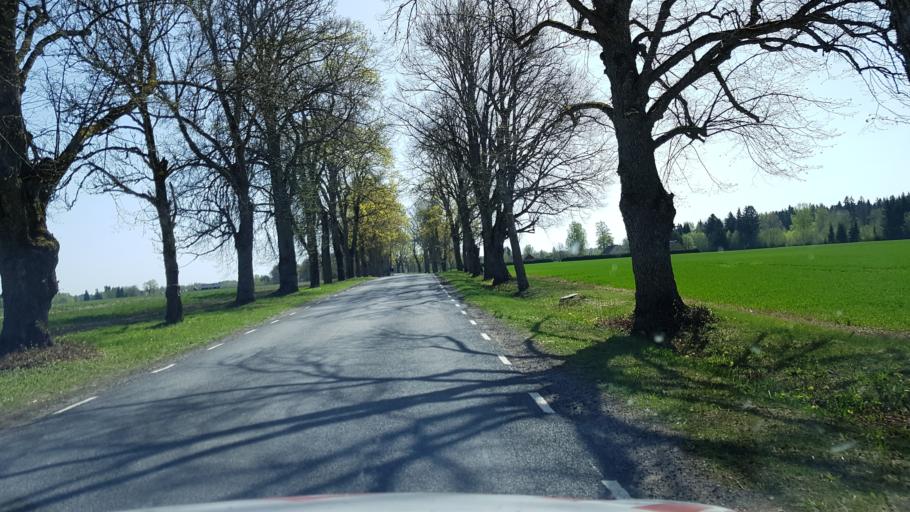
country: EE
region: Viljandimaa
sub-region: Vohma linn
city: Vohma
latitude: 58.5453
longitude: 25.5689
